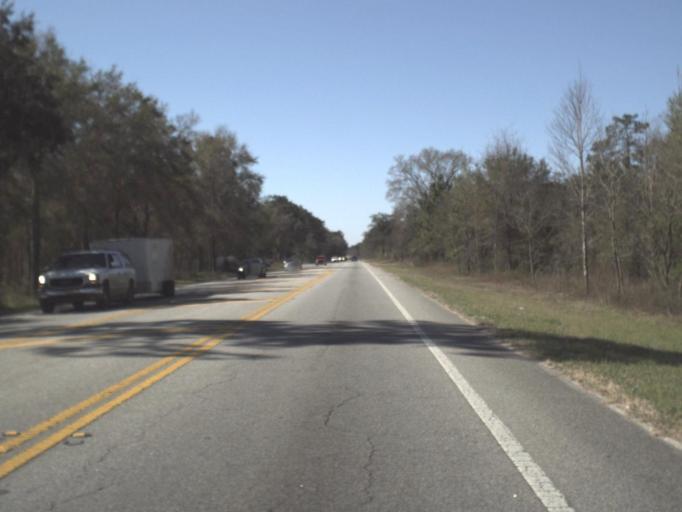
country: US
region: Florida
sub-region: Leon County
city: Woodville
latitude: 30.3309
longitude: -84.3268
